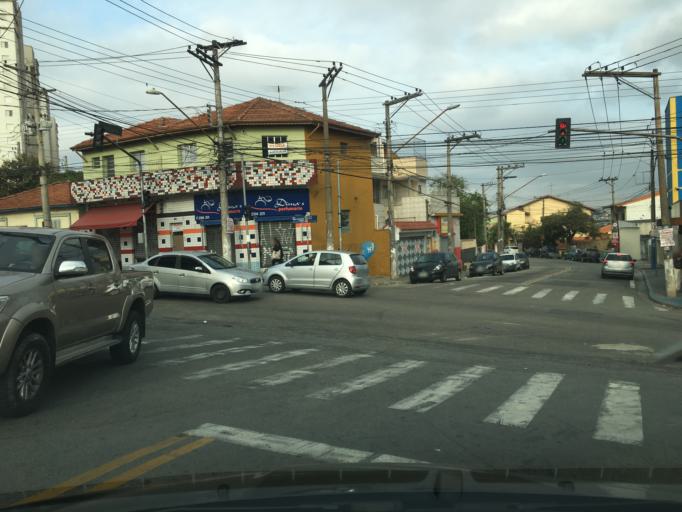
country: BR
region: Sao Paulo
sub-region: Guarulhos
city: Guarulhos
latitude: -23.5013
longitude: -46.5553
